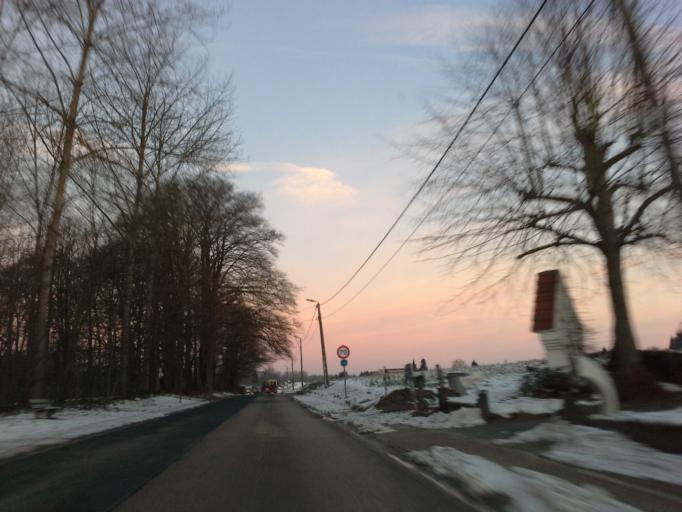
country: BE
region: Flanders
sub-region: Provincie Vlaams-Brabant
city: Lubbeek
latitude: 50.8819
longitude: 4.8557
